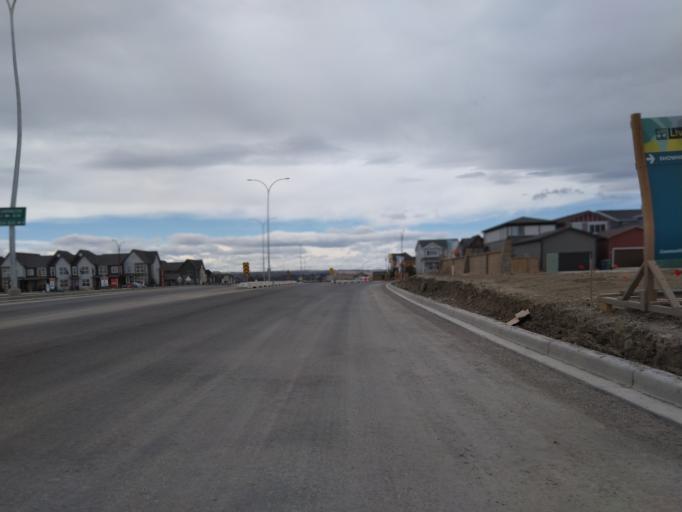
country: CA
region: Alberta
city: Airdrie
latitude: 51.1835
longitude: -114.0742
